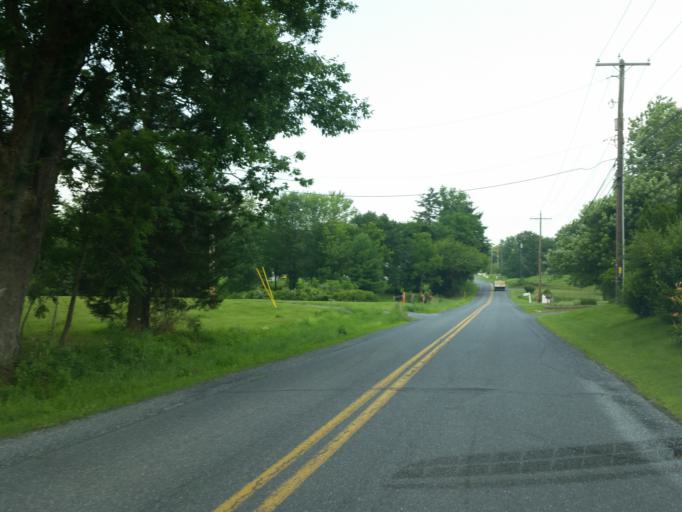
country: US
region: Pennsylvania
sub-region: Lebanon County
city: Palmyra
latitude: 40.3831
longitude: -76.6399
